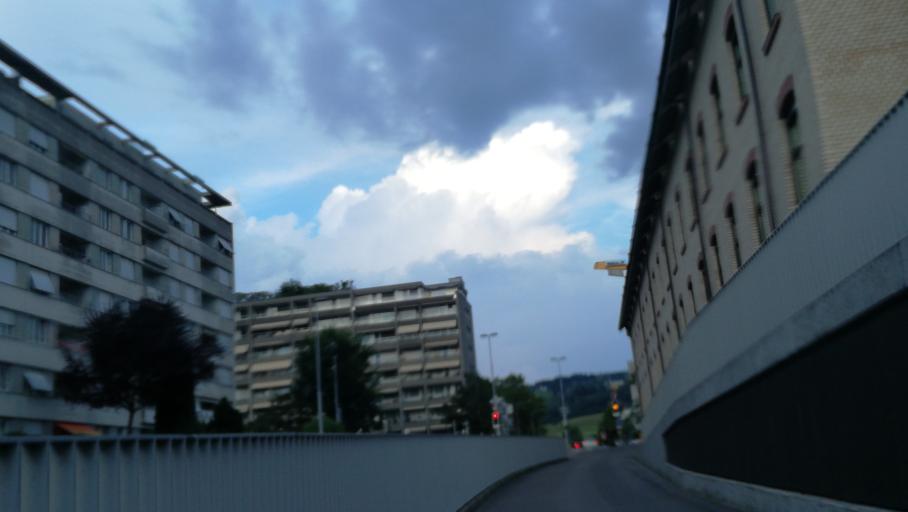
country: CH
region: Zug
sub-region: Zug
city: Zug
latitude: 47.1799
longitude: 8.5174
